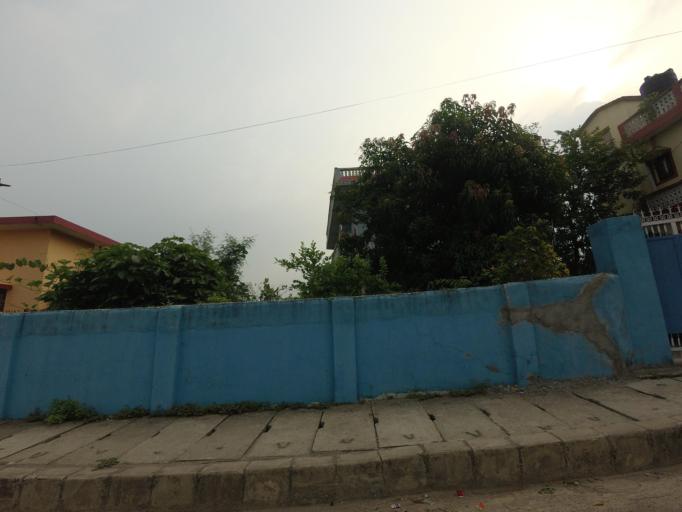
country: NP
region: Western Region
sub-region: Lumbini Zone
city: Bhairahawa
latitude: 27.5252
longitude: 83.4525
